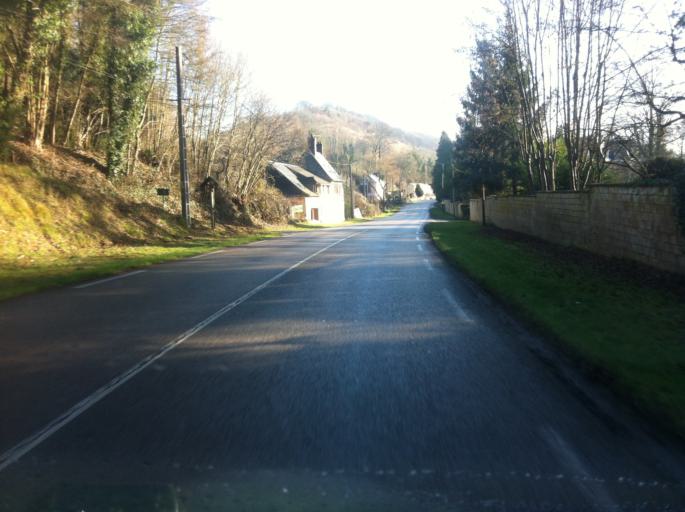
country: FR
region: Haute-Normandie
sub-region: Departement de la Seine-Maritime
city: Saint-Pierre-de-Varengeville
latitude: 49.4852
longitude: 0.9208
